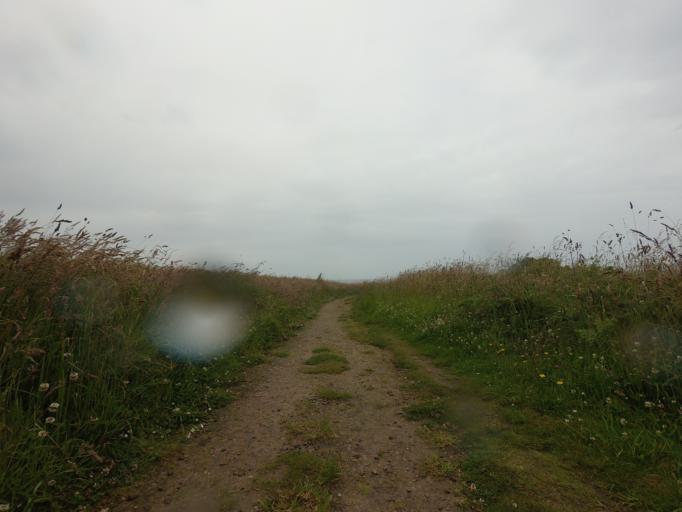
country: GB
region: Scotland
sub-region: Moray
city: Portknockie
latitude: 57.7025
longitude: -2.8744
